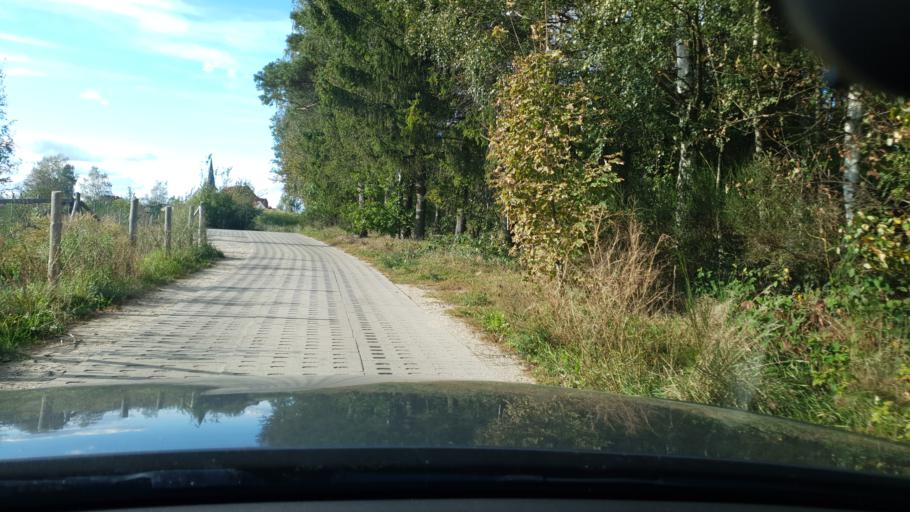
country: PL
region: Pomeranian Voivodeship
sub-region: Powiat kartuski
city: Chwaszczyno
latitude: 54.4836
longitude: 18.4241
